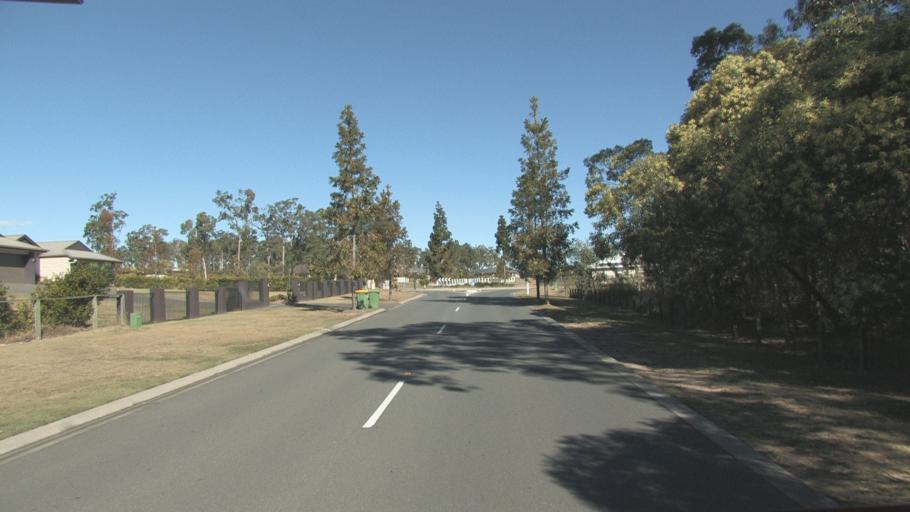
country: AU
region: Queensland
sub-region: Logan
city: North Maclean
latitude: -27.7569
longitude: 152.9497
